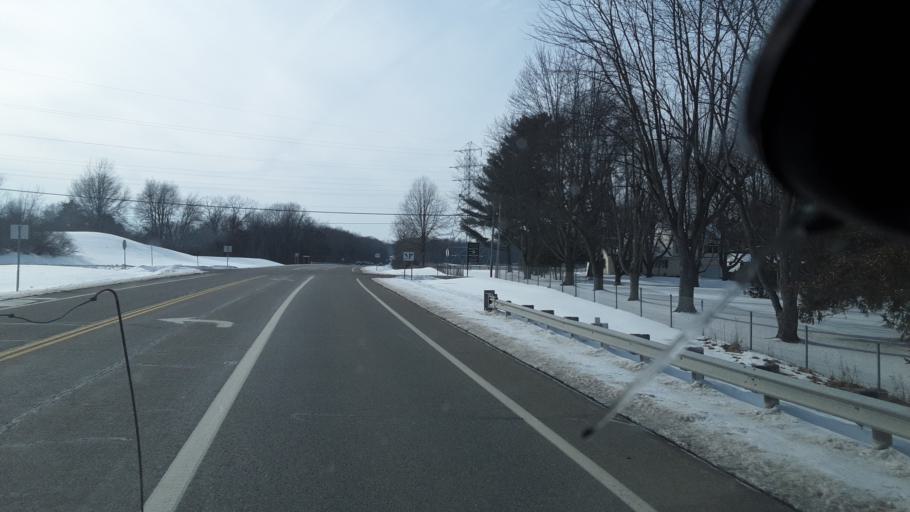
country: US
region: Ohio
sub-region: Stark County
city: Hartville
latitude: 41.0268
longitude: -81.3282
